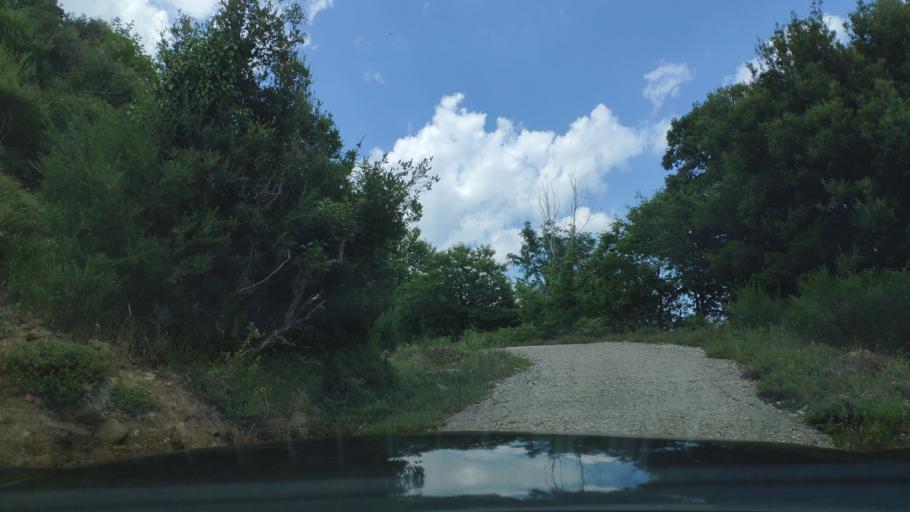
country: GR
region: Epirus
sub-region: Nomos Artas
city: Agios Dimitrios
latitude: 39.3185
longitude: 21.0005
